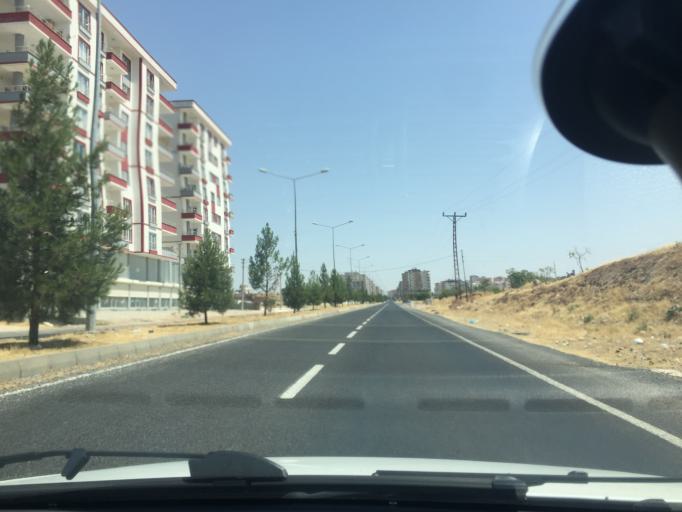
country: TR
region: Mardin
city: Midyat
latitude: 37.4364
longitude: 41.3184
